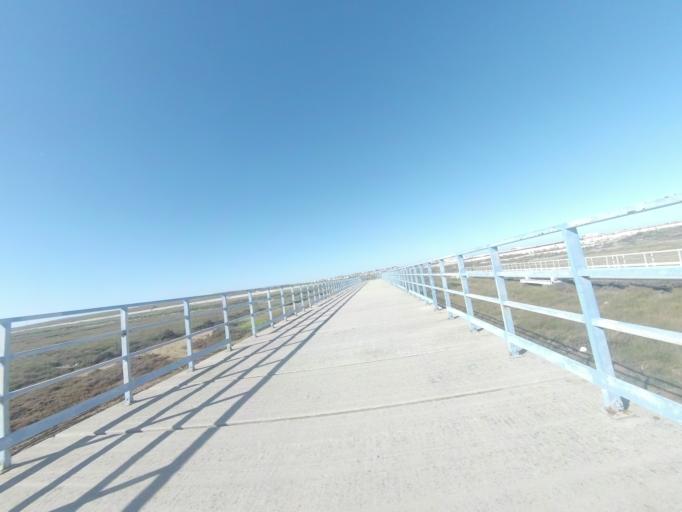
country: ES
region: Andalusia
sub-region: Provincia de Huelva
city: Palos de la Frontera
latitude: 37.2505
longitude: -6.9009
